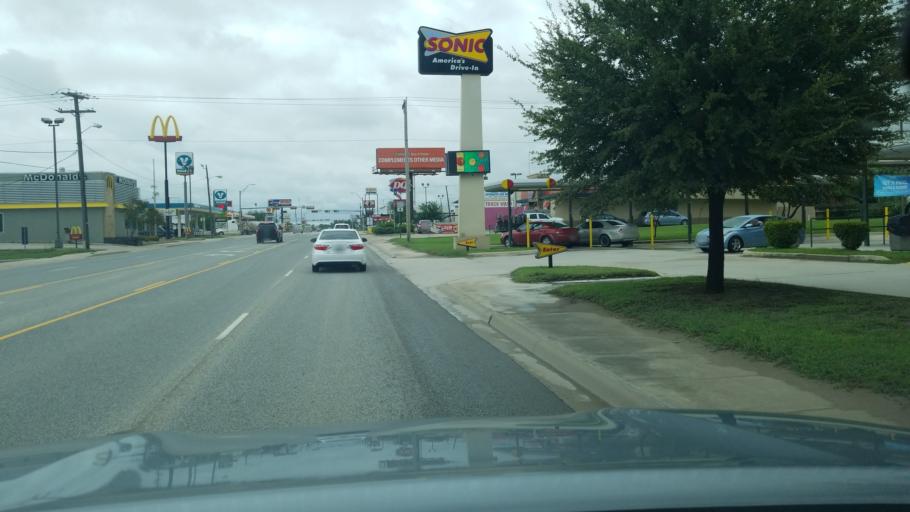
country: US
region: Texas
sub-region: Dimmit County
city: Carrizo Springs
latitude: 28.5244
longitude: -99.8559
